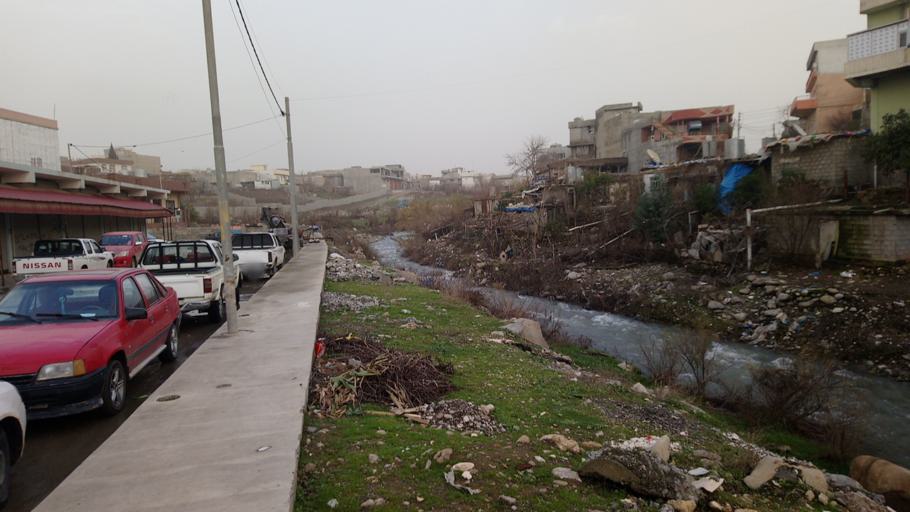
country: IQ
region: As Sulaymaniyah
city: Qeladize
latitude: 36.1794
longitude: 45.1283
